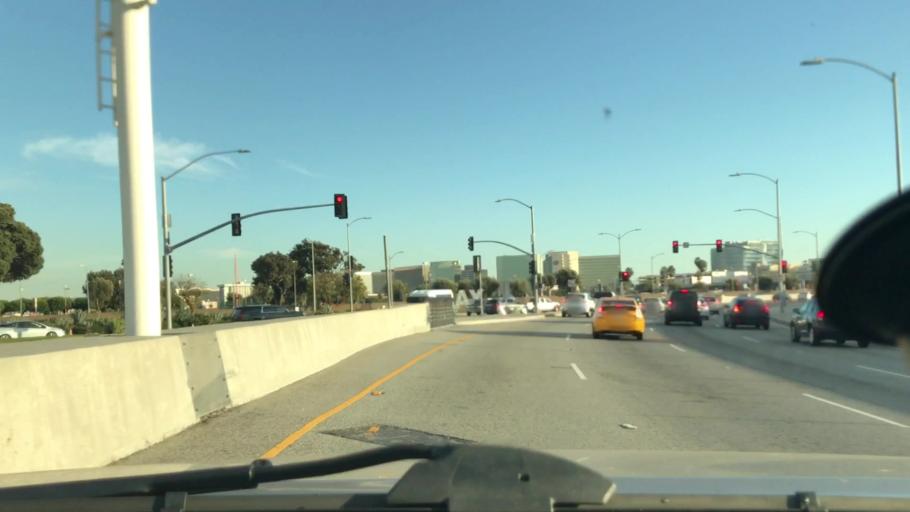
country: US
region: California
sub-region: Los Angeles County
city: El Segundo
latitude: 33.9526
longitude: -118.3970
